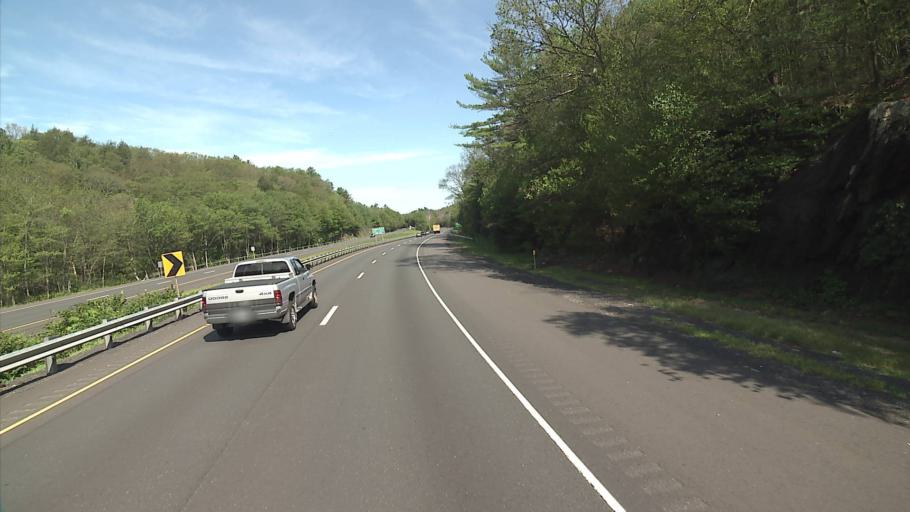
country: US
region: Connecticut
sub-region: Hartford County
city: Terramuggus
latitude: 41.6531
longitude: -72.5004
